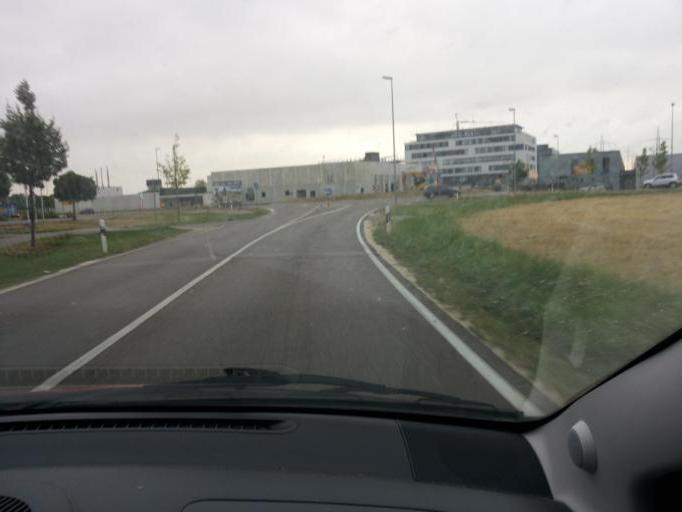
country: DE
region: Bavaria
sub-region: Upper Bavaria
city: Gaimersheim
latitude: 48.7897
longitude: 11.3759
